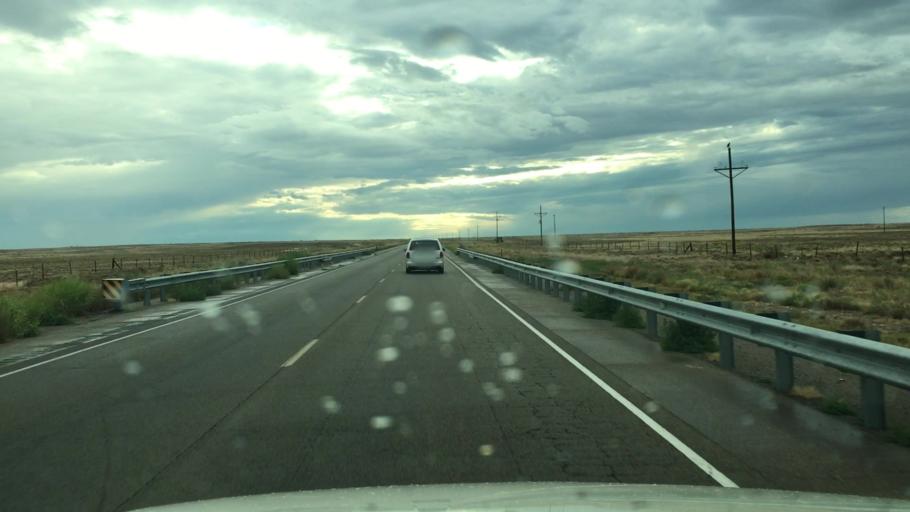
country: US
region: New Mexico
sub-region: Chaves County
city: Roswell
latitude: 33.4055
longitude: -104.3077
